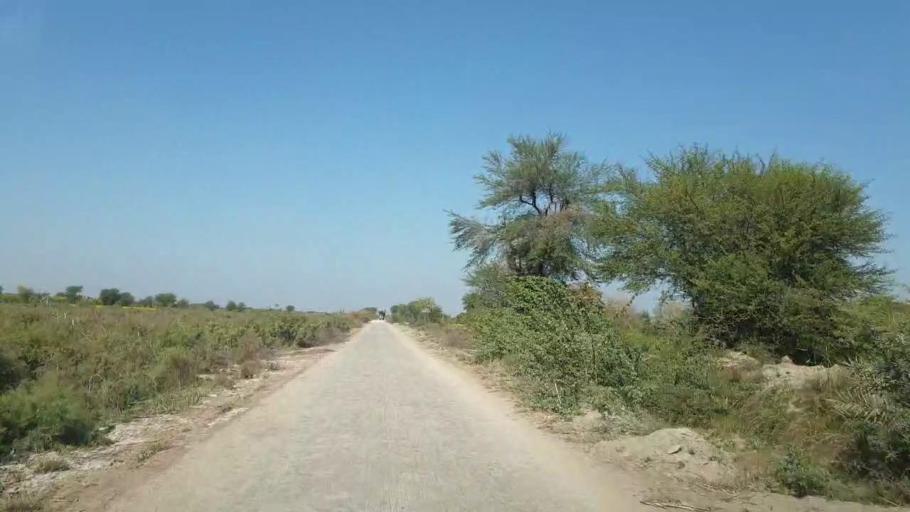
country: PK
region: Sindh
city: Mirpur Khas
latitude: 25.6596
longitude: 69.0270
